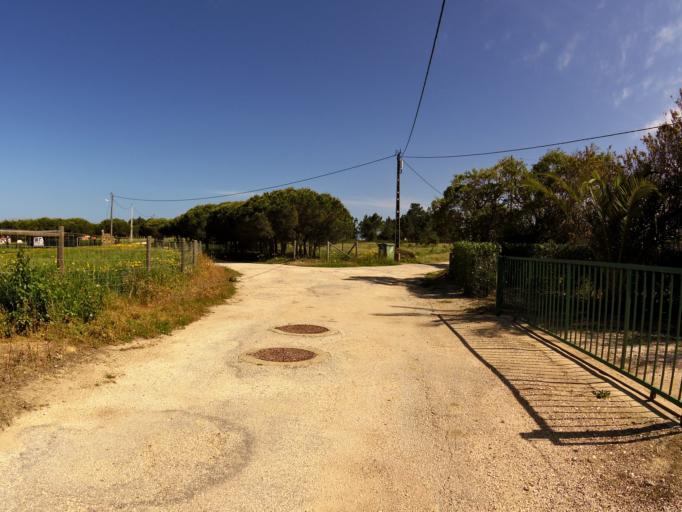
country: PT
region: Faro
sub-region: Aljezur
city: Aljezur
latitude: 37.3357
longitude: -8.8087
